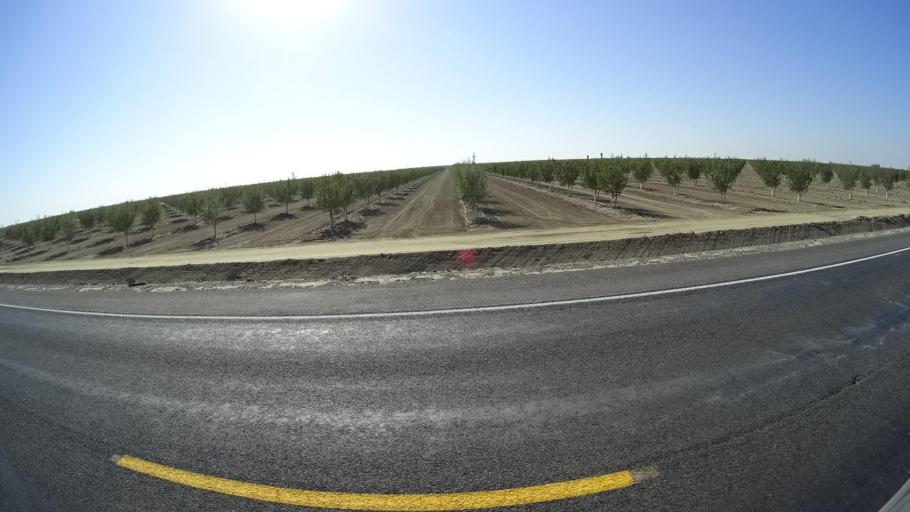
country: US
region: California
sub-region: Kern County
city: Delano
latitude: 35.7178
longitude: -119.2953
